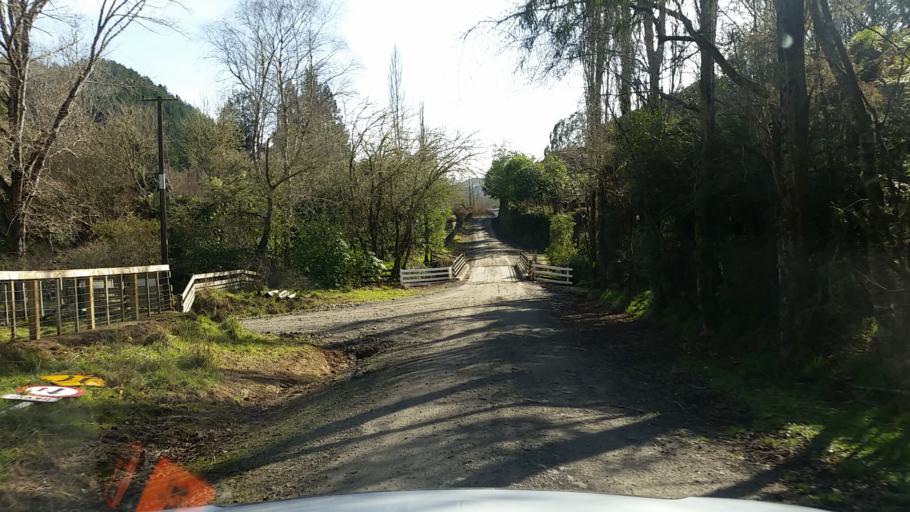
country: NZ
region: Taranaki
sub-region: South Taranaki District
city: Eltham
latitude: -39.3596
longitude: 174.5128
